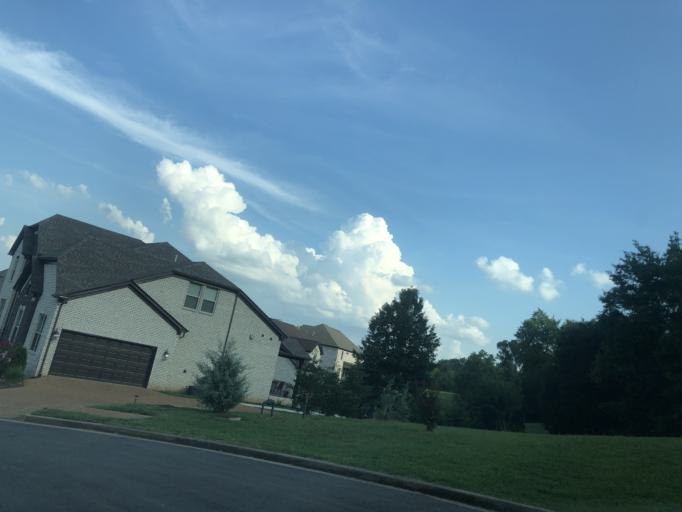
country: US
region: Tennessee
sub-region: Davidson County
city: Nashville
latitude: 36.2556
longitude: -86.8343
